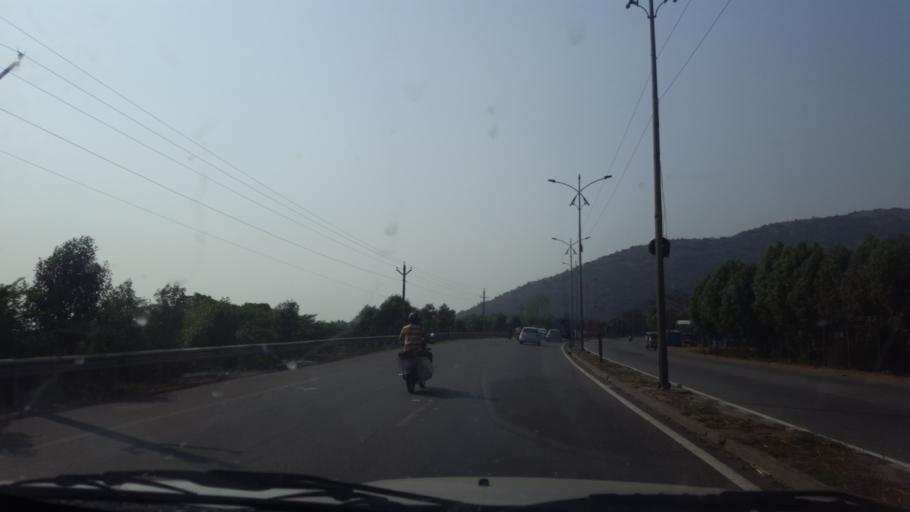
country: IN
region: Andhra Pradesh
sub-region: Vishakhapatnam
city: Anakapalle
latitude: 17.6875
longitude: 83.0777
